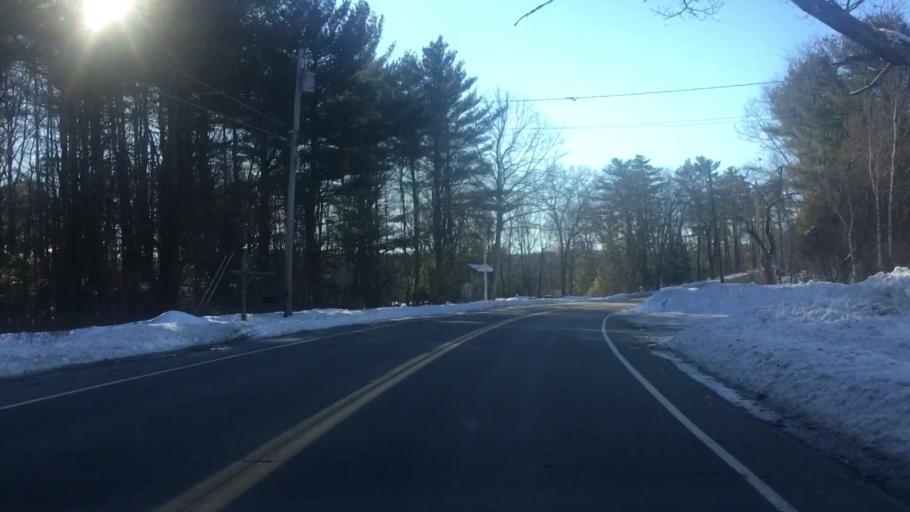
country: US
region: Maine
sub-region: Somerset County
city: Madison
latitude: 44.8188
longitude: -69.8786
